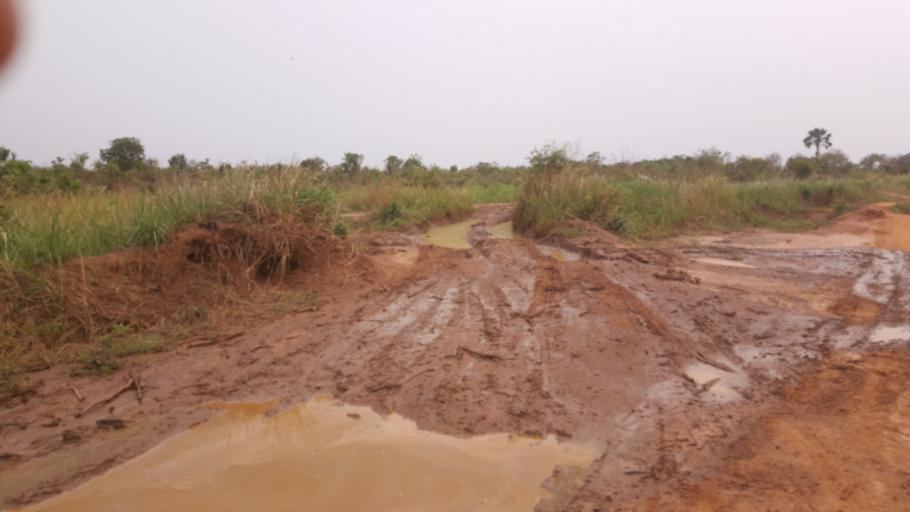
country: CD
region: Bandundu
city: Bandundu
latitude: -3.4679
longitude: 17.7138
